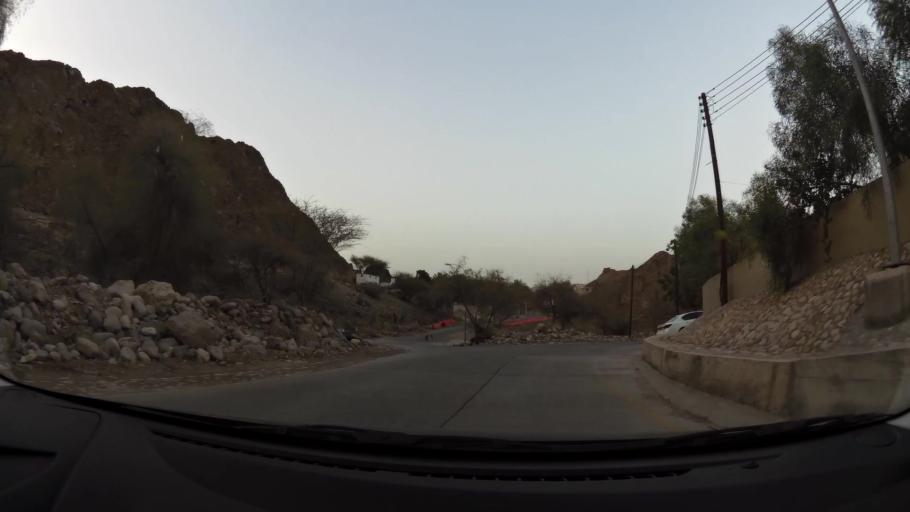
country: OM
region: Muhafazat Masqat
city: Bawshar
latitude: 23.4778
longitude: 58.3263
